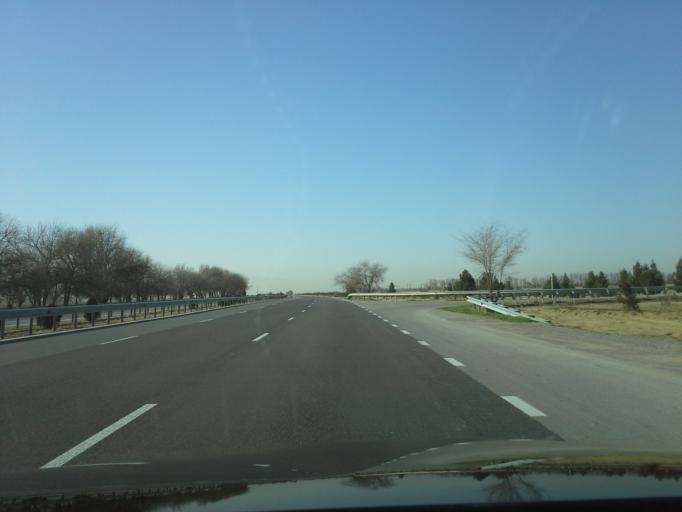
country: TM
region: Ahal
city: Annau
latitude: 37.9010
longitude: 58.5738
